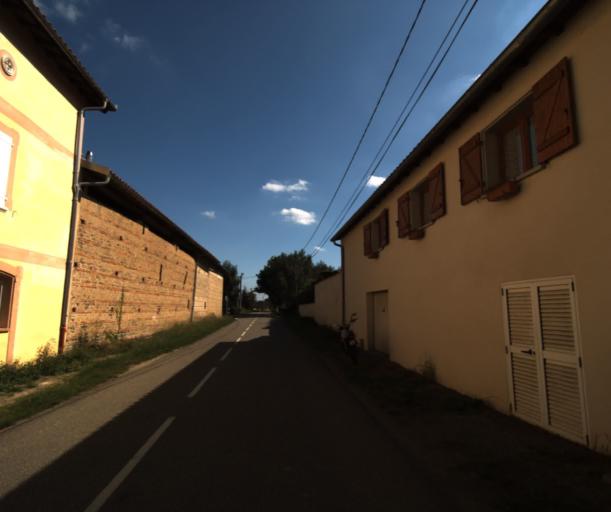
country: FR
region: Midi-Pyrenees
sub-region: Departement de la Haute-Garonne
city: Fonsorbes
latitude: 43.5065
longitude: 1.2197
